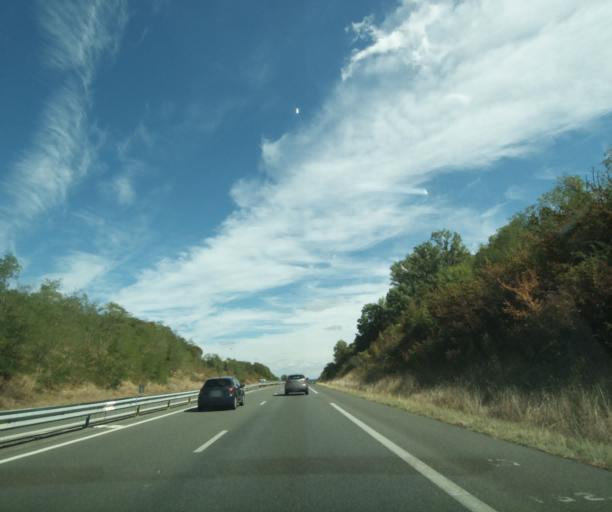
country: FR
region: Midi-Pyrenees
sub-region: Departement du Tarn-et-Garonne
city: Auvillar
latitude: 44.0597
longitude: 0.9047
